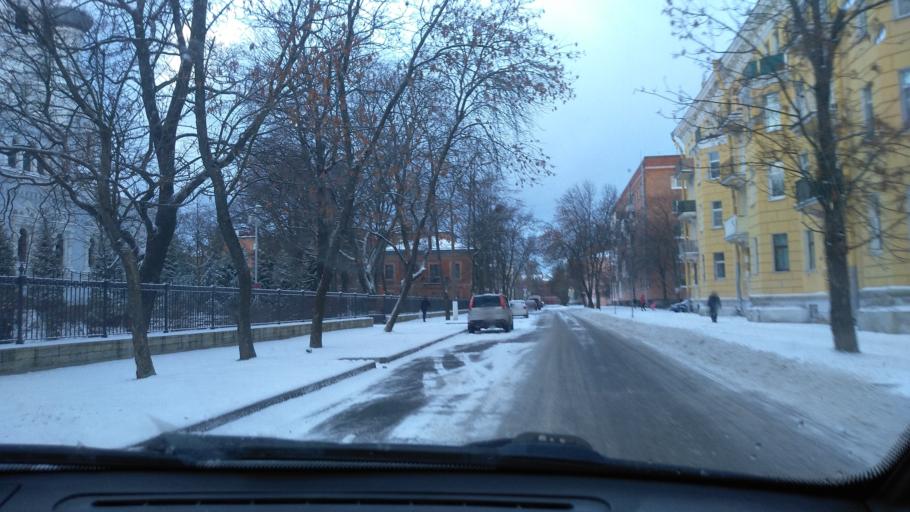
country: RU
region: St.-Petersburg
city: Kronshtadt
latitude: 59.9987
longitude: 29.7677
